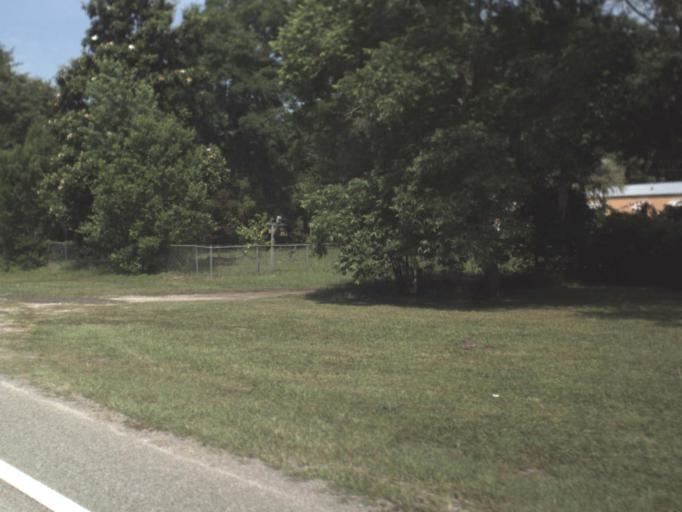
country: US
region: Florida
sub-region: Alachua County
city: Waldo
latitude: 29.7341
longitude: -82.2444
